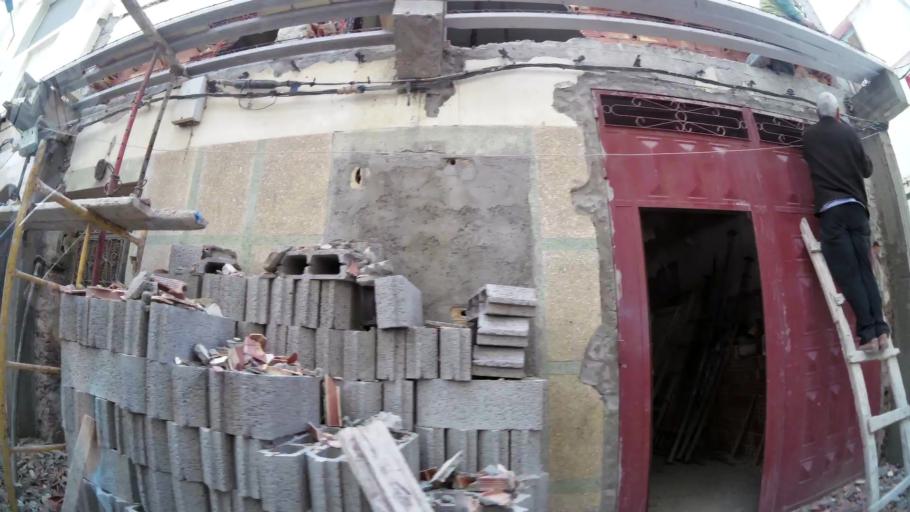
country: MA
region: Oriental
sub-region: Nador
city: Nador
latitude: 35.1697
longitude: -2.9320
